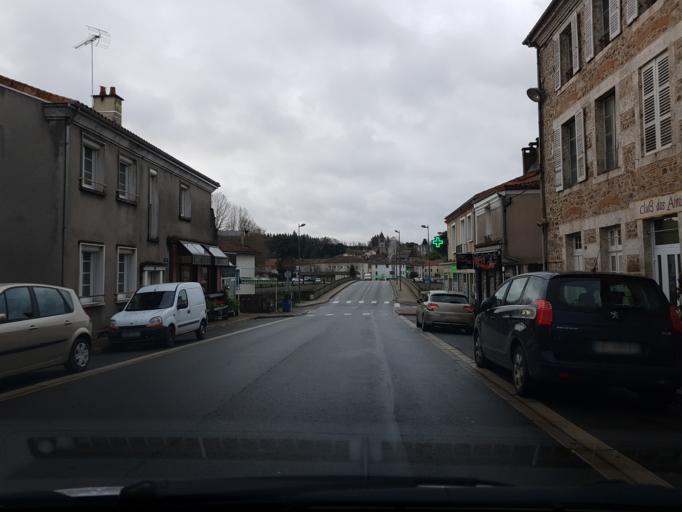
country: FR
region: Poitou-Charentes
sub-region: Departement de la Charente
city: Chabanais
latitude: 45.8760
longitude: 0.7197
